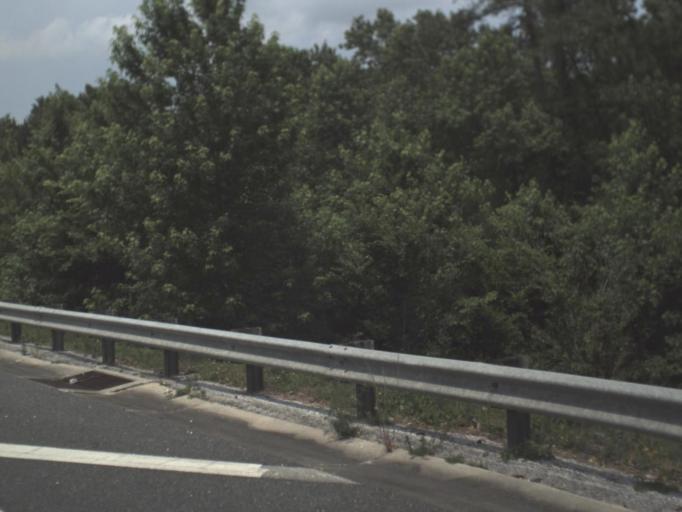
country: US
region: Florida
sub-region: Putnam County
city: Palatka
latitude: 29.6952
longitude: -81.6631
